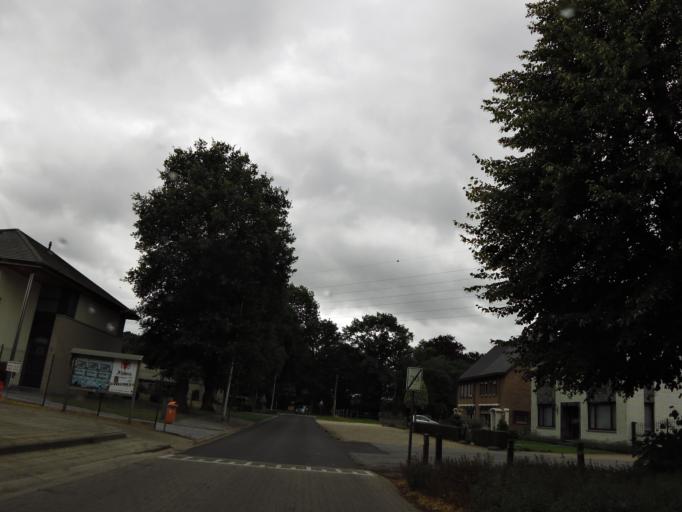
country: BE
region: Flanders
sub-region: Provincie Limburg
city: Maaseik
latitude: 51.0978
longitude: 5.7587
